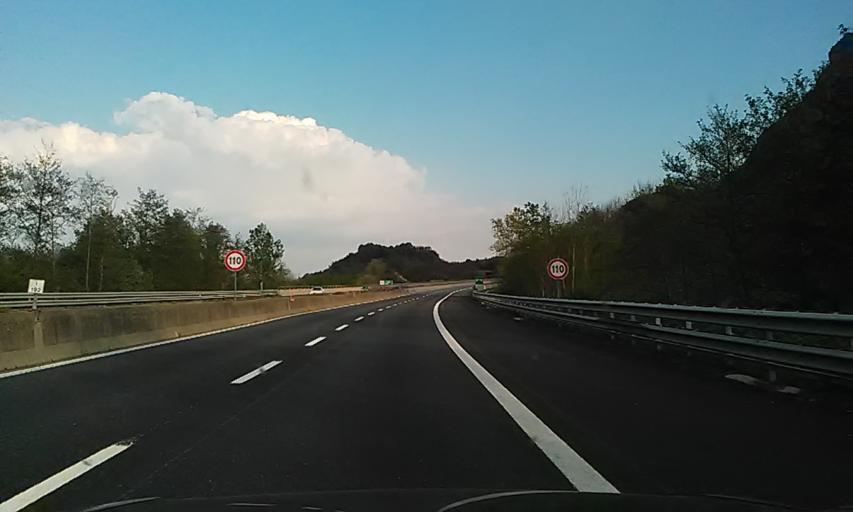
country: IT
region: Piedmont
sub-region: Provincia Verbano-Cusio-Ossola
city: Mergozzo
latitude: 45.9317
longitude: 8.4678
